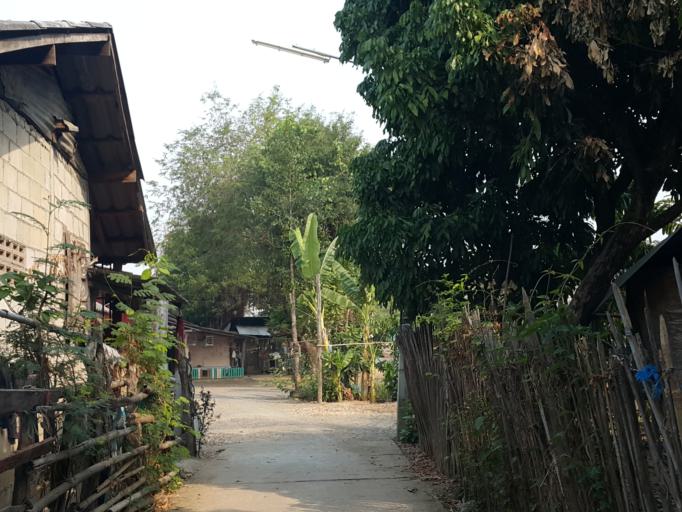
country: TH
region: Chiang Mai
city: San Kamphaeng
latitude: 18.7436
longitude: 99.0794
